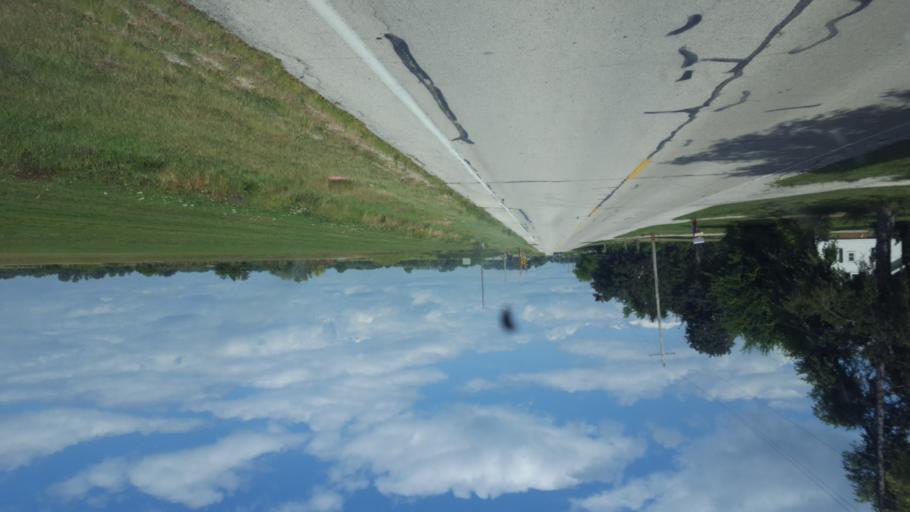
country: US
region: Ohio
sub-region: Lucas County
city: Curtice
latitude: 41.6443
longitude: -83.2733
